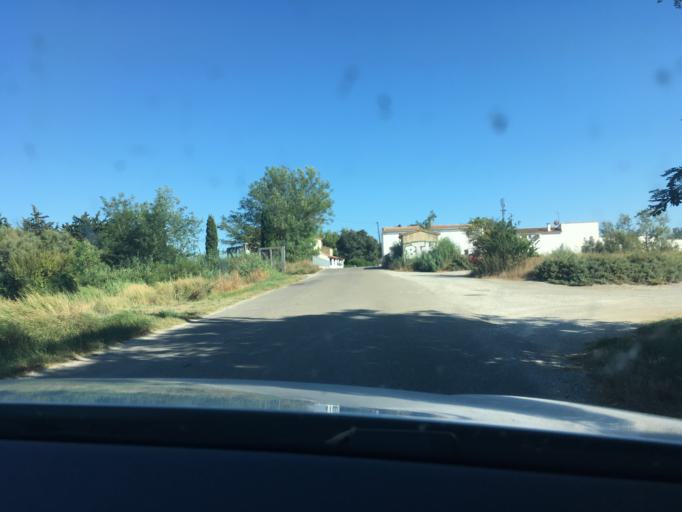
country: FR
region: Provence-Alpes-Cote d'Azur
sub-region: Departement des Bouches-du-Rhone
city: Saintes-Maries-de-la-Mer
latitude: 43.5451
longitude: 4.3465
